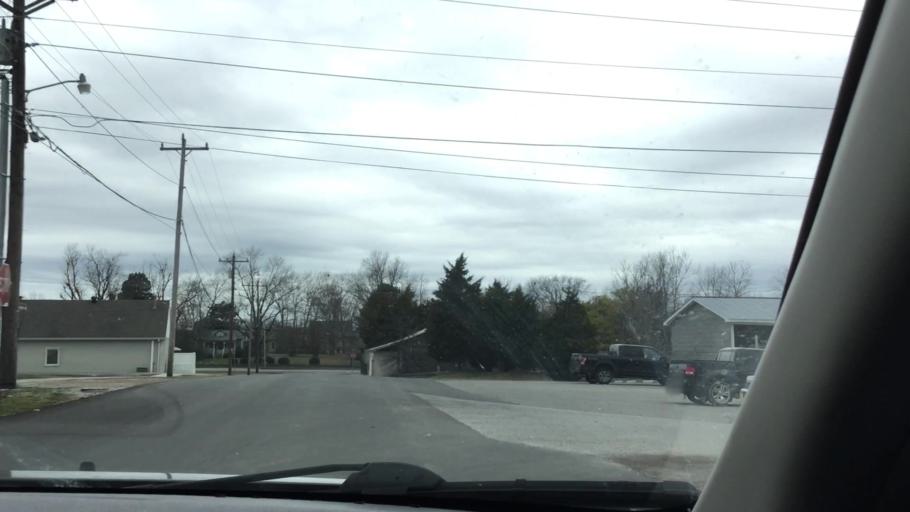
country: US
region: Tennessee
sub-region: Lewis County
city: Hohenwald
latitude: 35.5458
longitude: -87.5494
